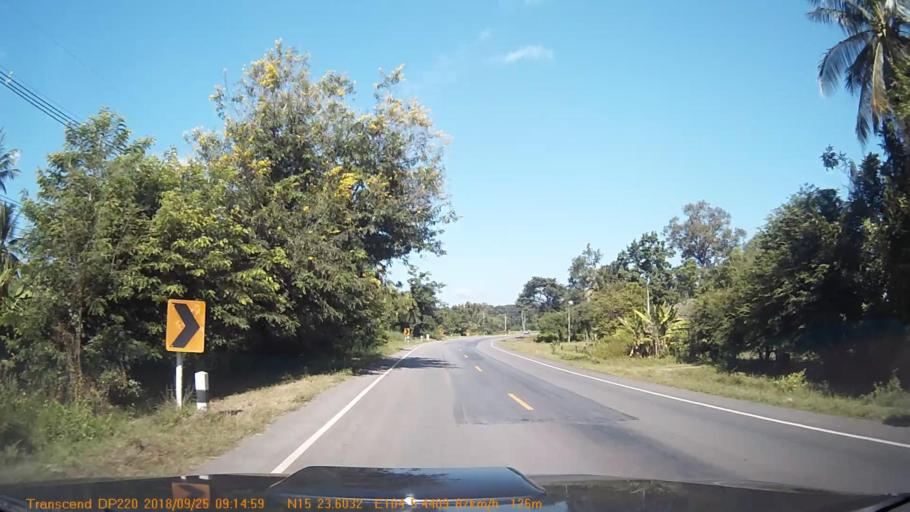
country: TH
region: Sisaket
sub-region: Amphoe Bueng Bun
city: Bueng Bun
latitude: 15.3934
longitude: 104.0905
